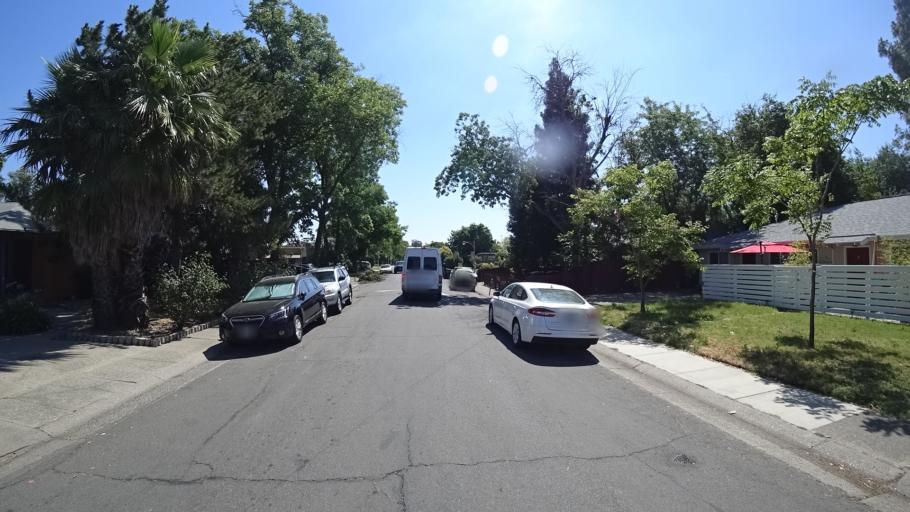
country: US
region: California
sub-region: Sacramento County
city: Sacramento
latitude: 38.5372
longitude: -121.4917
